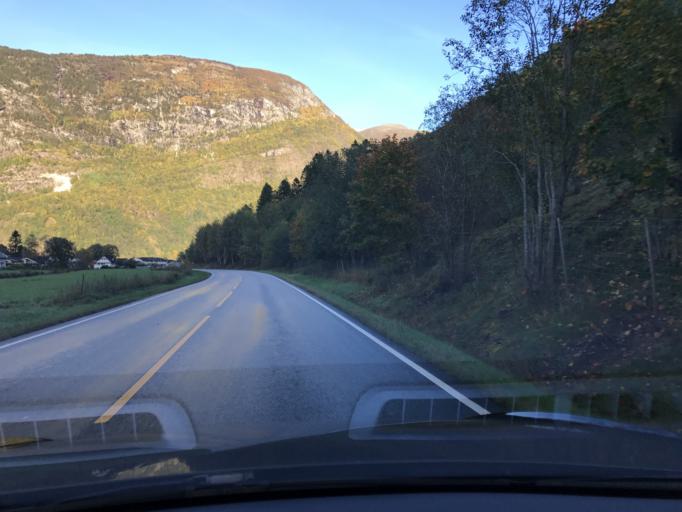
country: NO
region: Sogn og Fjordane
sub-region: Laerdal
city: Laerdalsoyri
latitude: 61.0968
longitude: 7.4948
